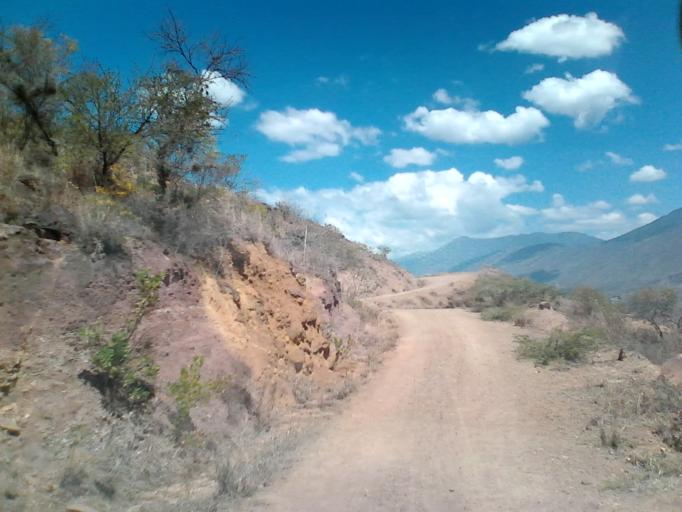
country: CO
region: Boyaca
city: Sachica
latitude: 5.5931
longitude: -73.5723
